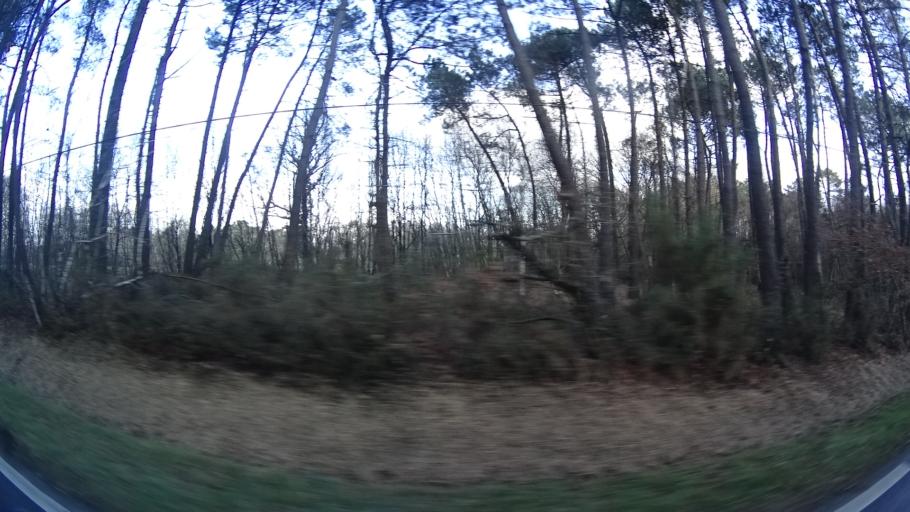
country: FR
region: Pays de la Loire
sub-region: Departement de la Loire-Atlantique
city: Guenrouet
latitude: 47.5668
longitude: -1.9711
